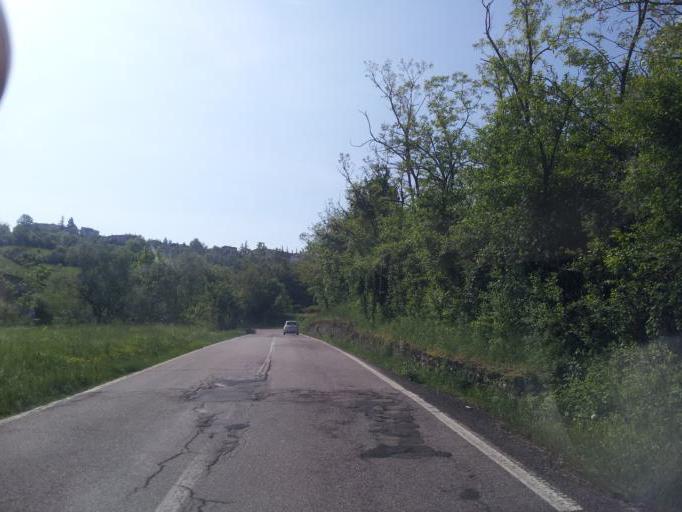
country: IT
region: Emilia-Romagna
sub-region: Provincia di Reggio Emilia
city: Villa Minozzo
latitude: 44.3692
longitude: 10.4615
